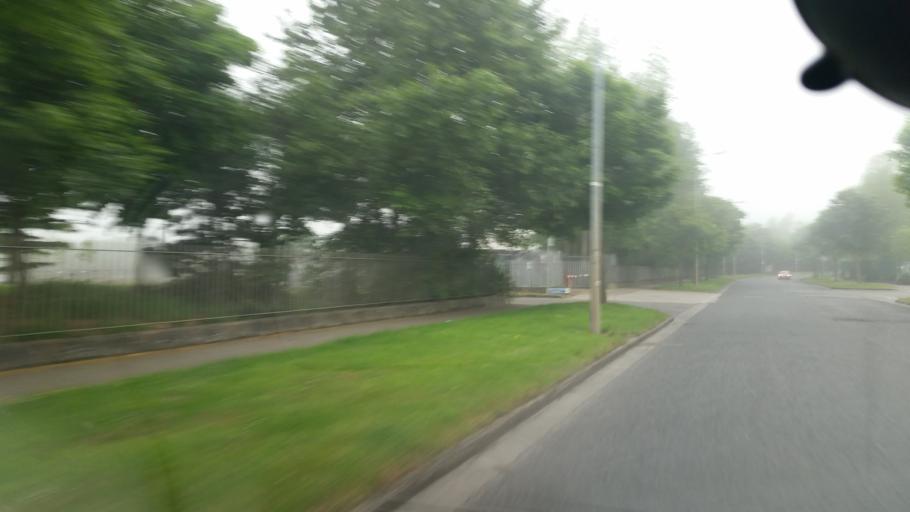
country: IE
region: Leinster
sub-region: Dublin City
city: Finglas
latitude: 53.4012
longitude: -6.2844
